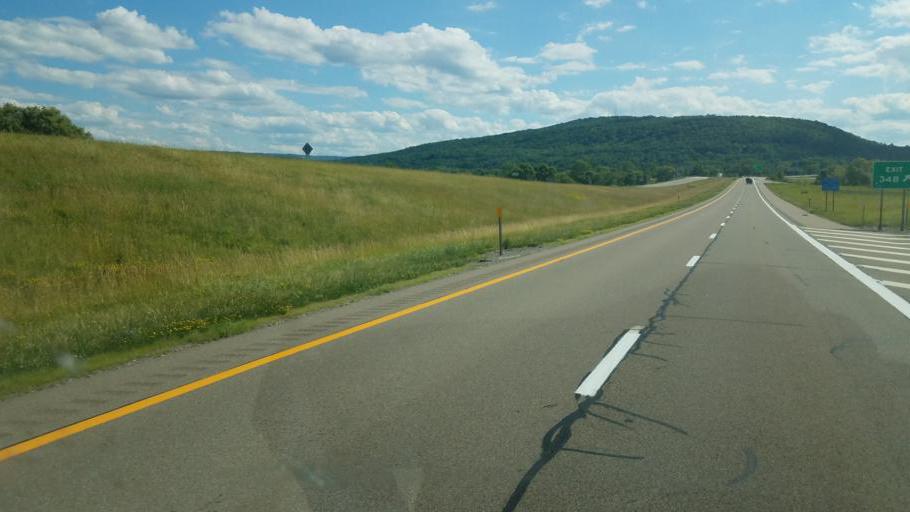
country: US
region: New York
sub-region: Steuben County
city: Hornell
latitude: 42.3745
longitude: -77.6725
